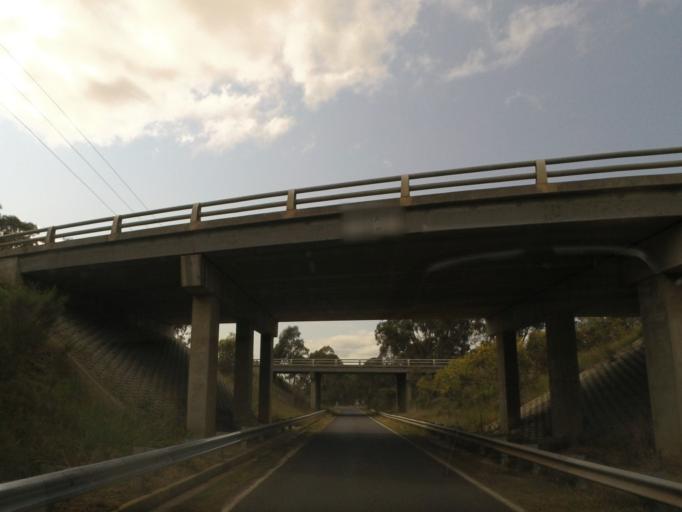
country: AU
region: Victoria
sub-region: Murrindindi
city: Kinglake West
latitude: -37.1077
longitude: 145.0915
